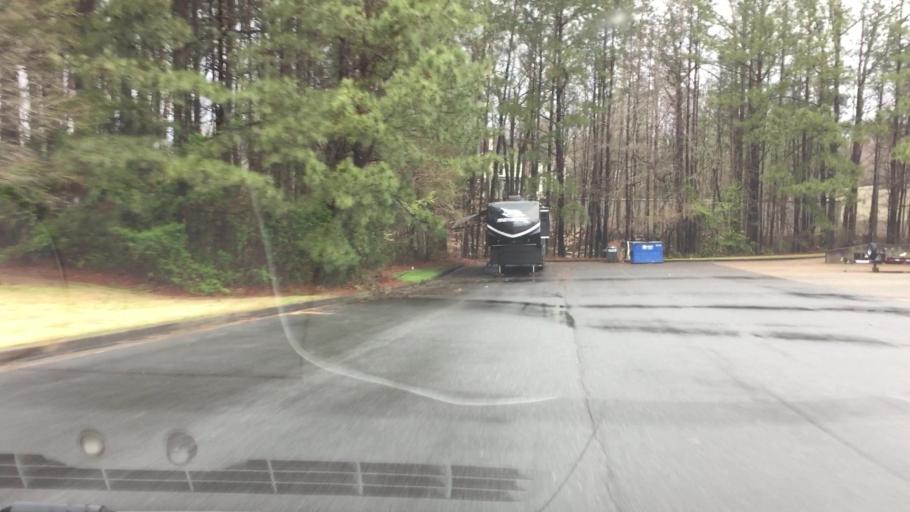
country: US
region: Georgia
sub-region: Fulton County
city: Milton
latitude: 34.1360
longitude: -84.2582
